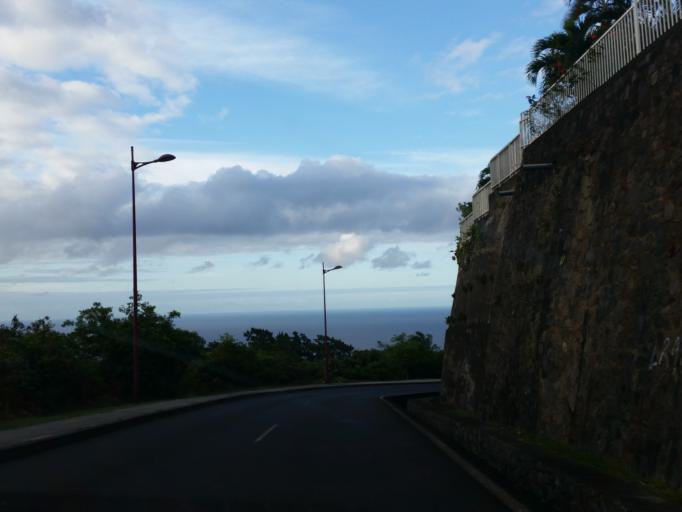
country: RE
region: Reunion
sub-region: Reunion
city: Saint-Denis
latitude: -20.8867
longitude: 55.4200
